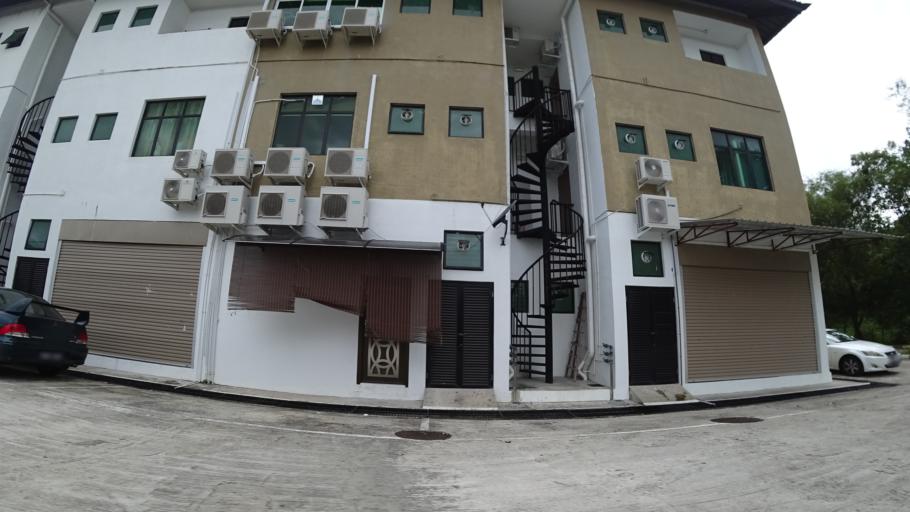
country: BN
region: Brunei and Muara
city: Bandar Seri Begawan
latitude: 4.9473
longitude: 114.9435
